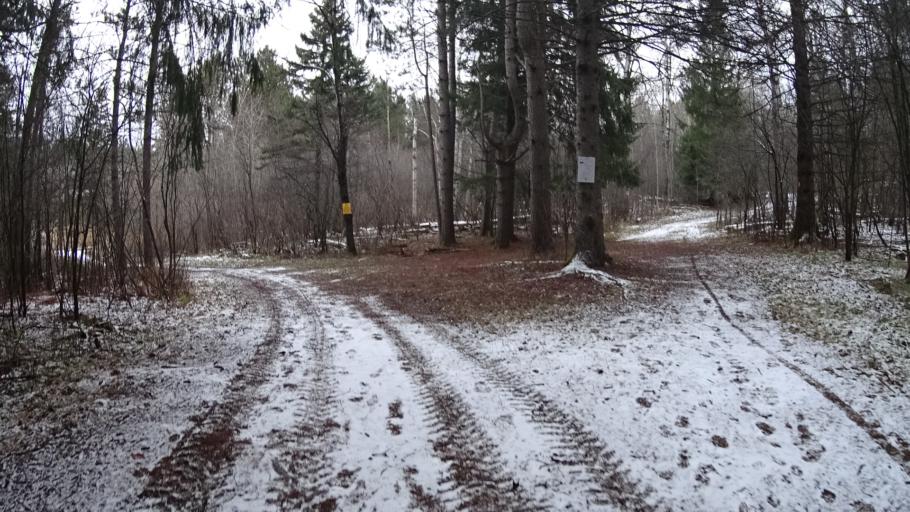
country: US
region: Minnesota
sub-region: Saint Louis County
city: Arnold
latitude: 46.8369
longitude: -92.0841
